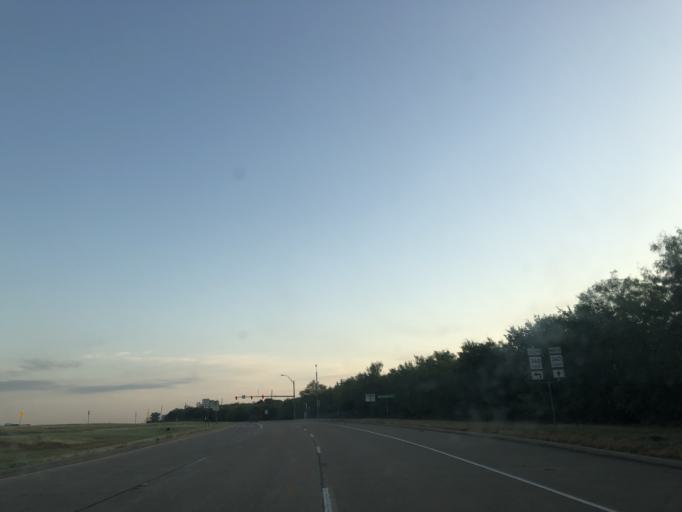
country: US
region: Texas
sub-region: Tarrant County
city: Euless
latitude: 32.8505
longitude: -97.0625
